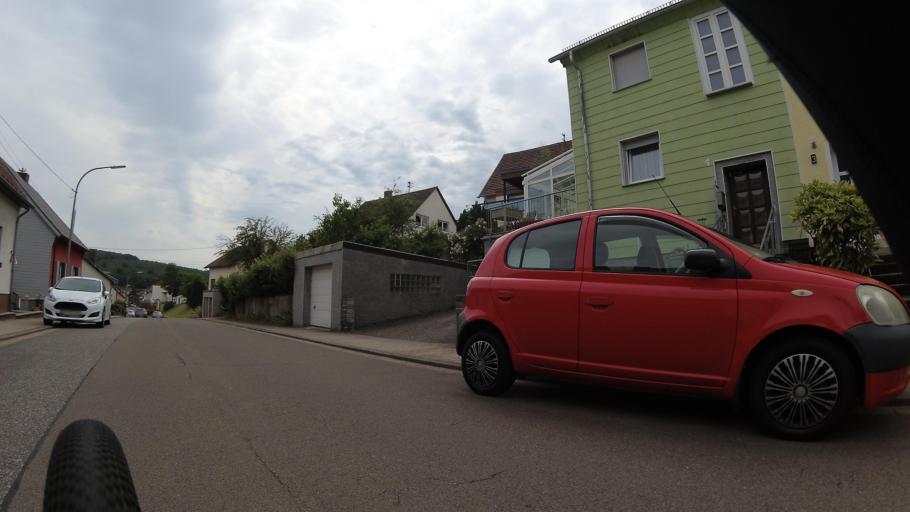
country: DE
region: Saarland
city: Quierschied
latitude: 49.3223
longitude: 7.0492
